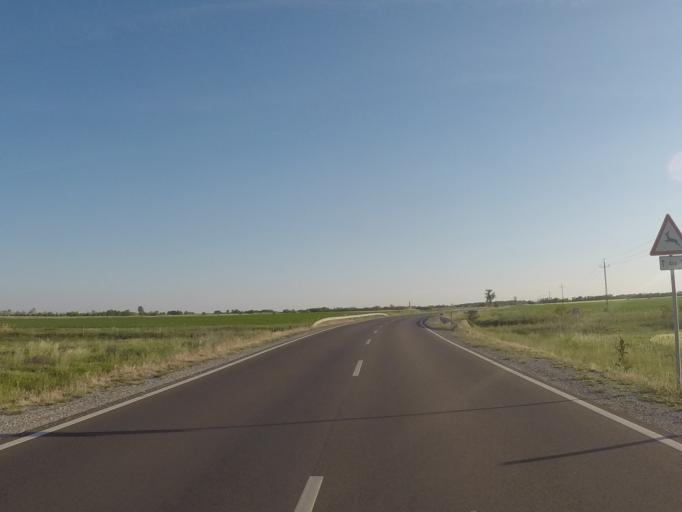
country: HU
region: Heves
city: Besenyotelek
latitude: 47.6844
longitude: 20.3866
